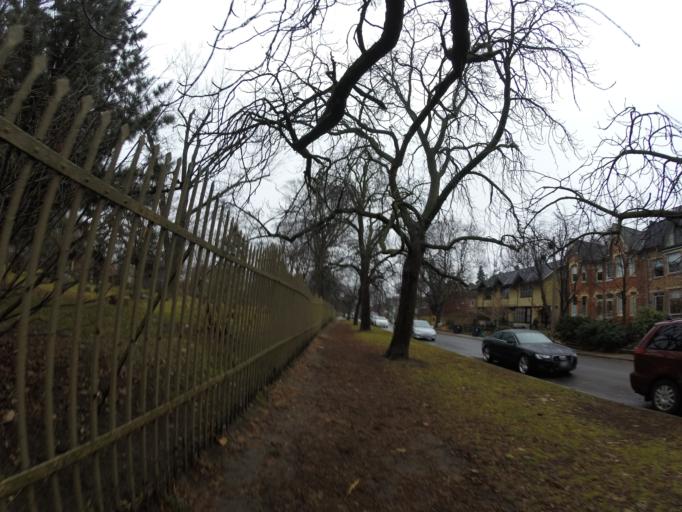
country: CA
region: Ontario
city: Toronto
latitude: 43.6679
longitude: -79.3634
